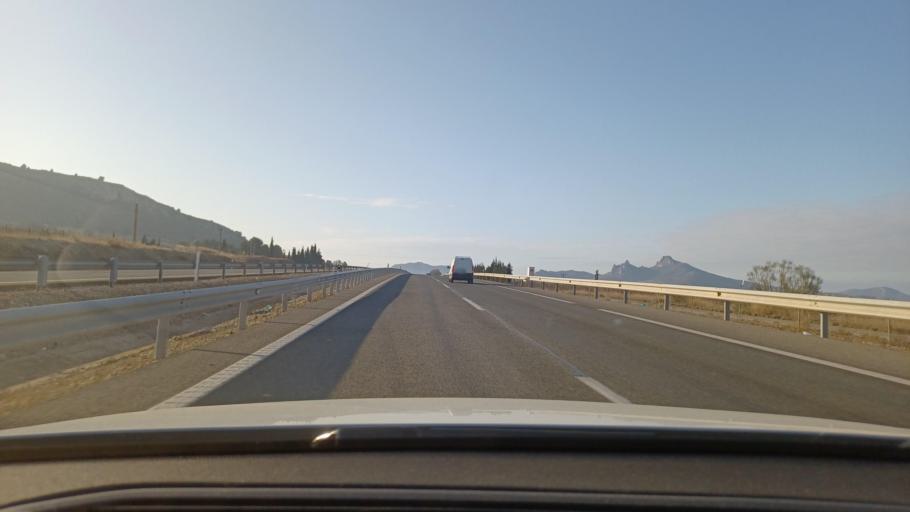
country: ES
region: Valencia
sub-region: Provincia de Alicante
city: Villena
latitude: 38.5948
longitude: -0.8445
